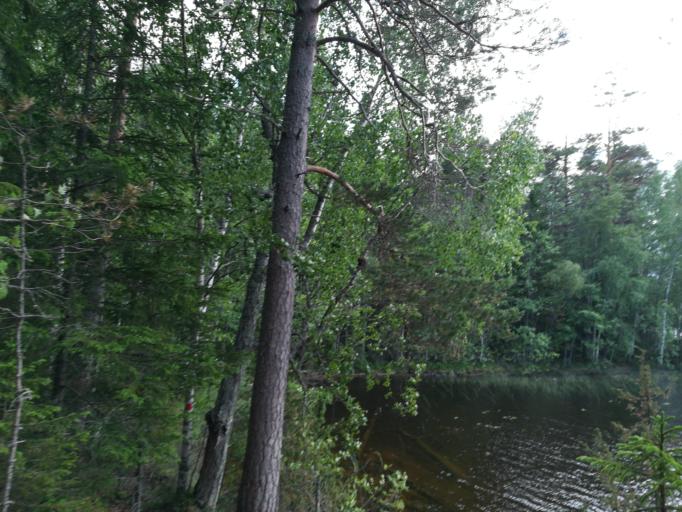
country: FI
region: South Karelia
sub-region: Lappeenranta
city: Savitaipale
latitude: 61.3051
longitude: 27.6142
